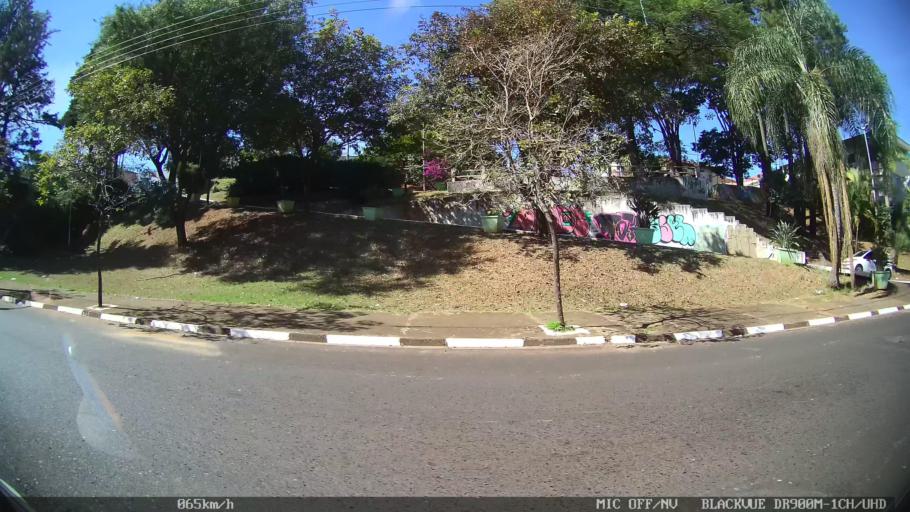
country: BR
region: Sao Paulo
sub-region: Franca
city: Franca
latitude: -20.5372
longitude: -47.4070
